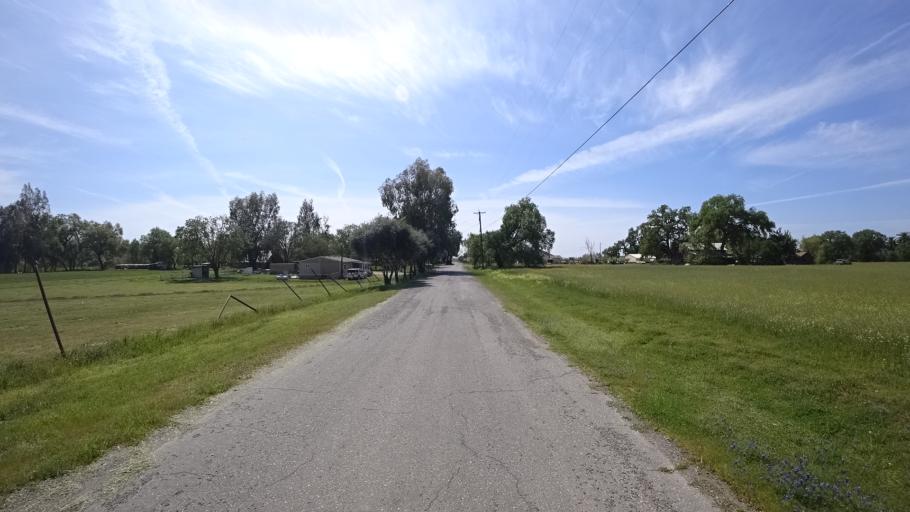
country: US
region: California
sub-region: Glenn County
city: Hamilton City
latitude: 39.7990
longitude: -122.0570
